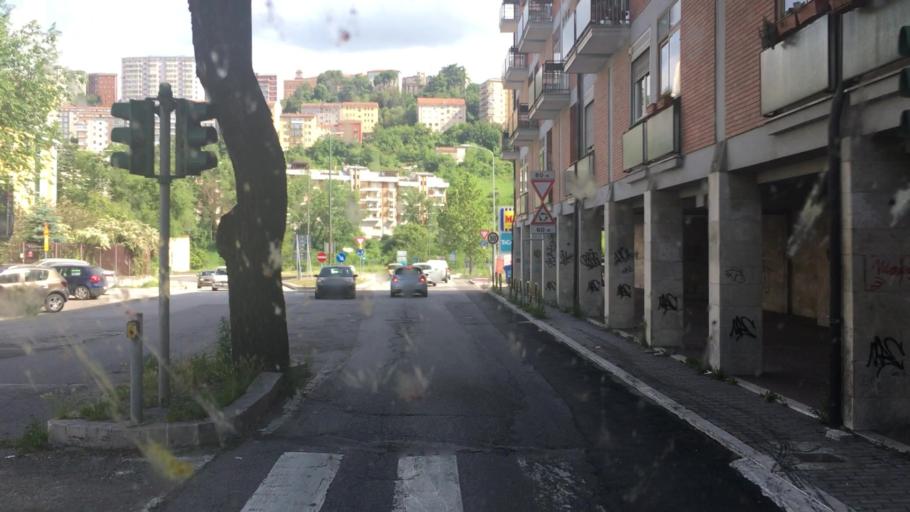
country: IT
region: Basilicate
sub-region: Provincia di Potenza
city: Potenza
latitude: 40.6437
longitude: 15.7990
